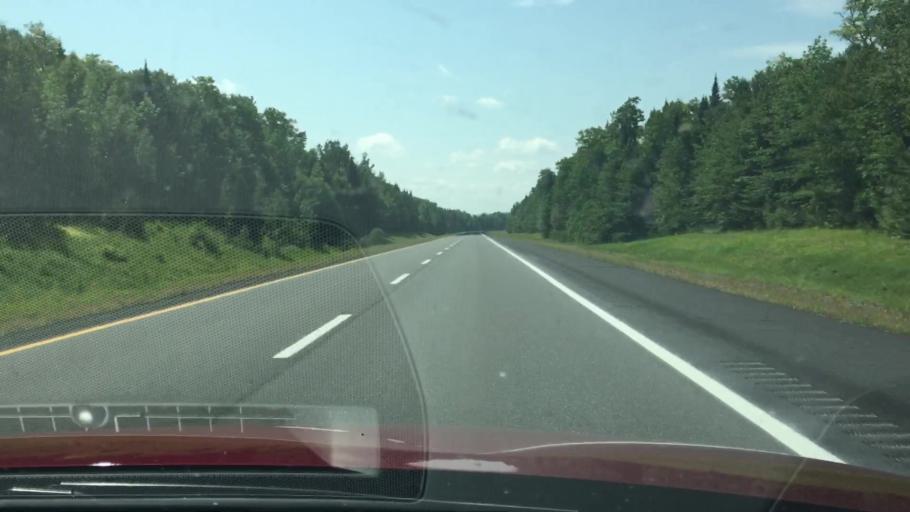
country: US
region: Maine
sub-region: Penobscot County
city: Patten
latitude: 45.9413
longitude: -68.3467
